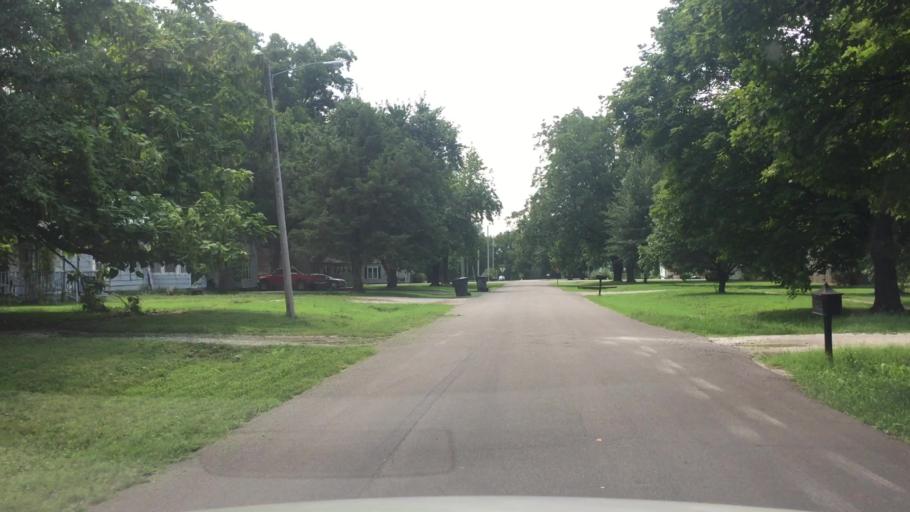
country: US
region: Kansas
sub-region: Labette County
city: Oswego
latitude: 37.1639
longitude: -95.1047
